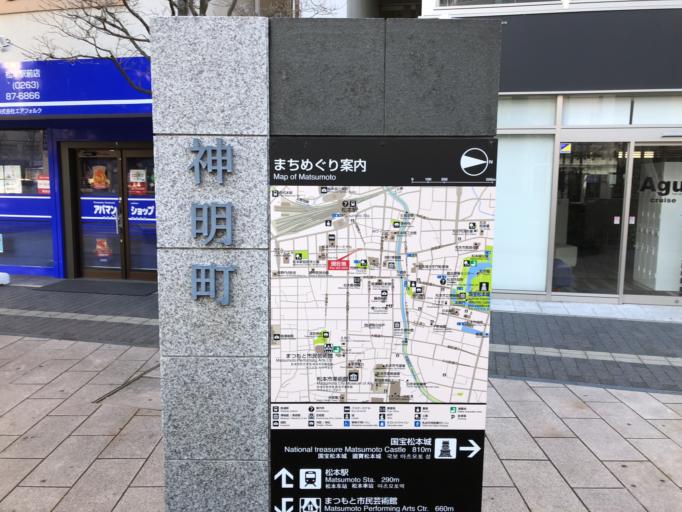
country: JP
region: Nagano
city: Matsumoto
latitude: 36.2316
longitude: 137.9674
